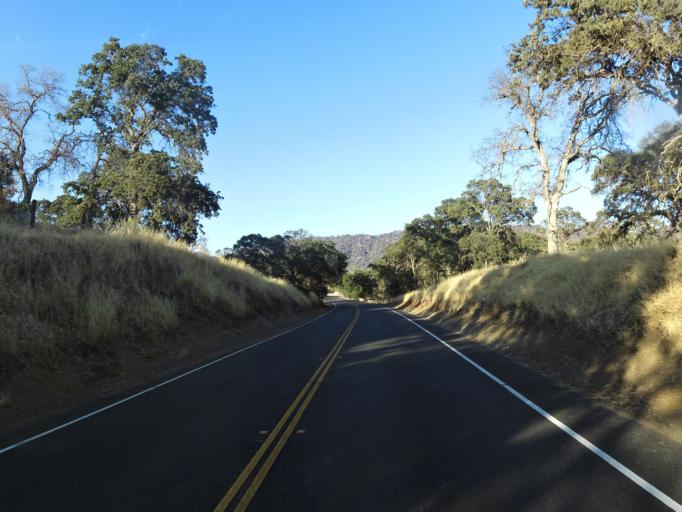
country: US
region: California
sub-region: Mariposa County
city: Mariposa
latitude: 37.4368
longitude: -120.0892
